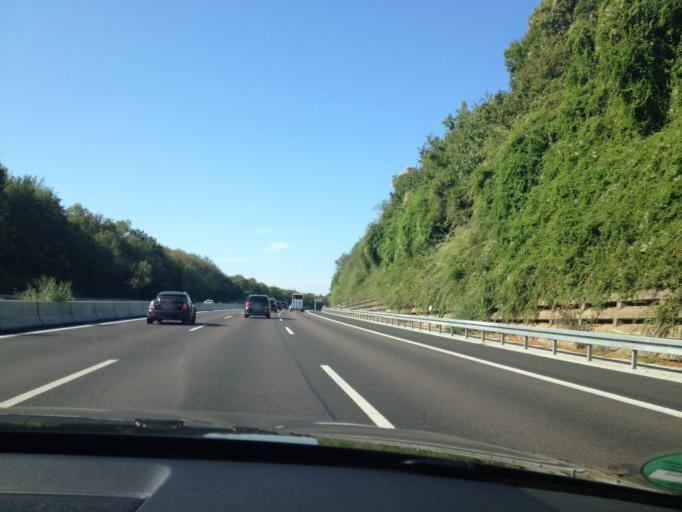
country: DE
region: Baden-Wuerttemberg
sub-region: Regierungsbezirk Stuttgart
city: Freiberg am Neckar
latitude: 48.9361
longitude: 9.1897
